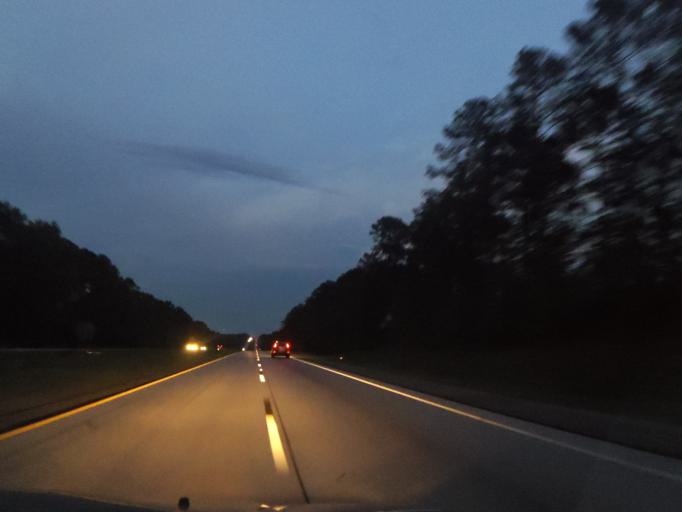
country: US
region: Georgia
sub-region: McDuffie County
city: Thomson
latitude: 33.5090
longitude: -82.4265
